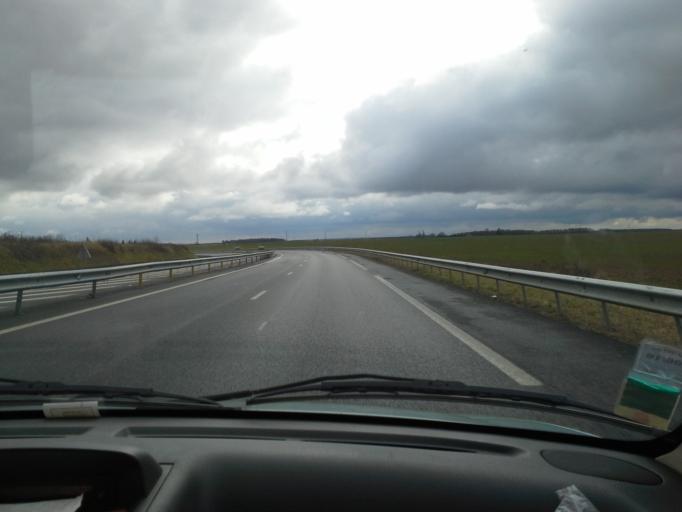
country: FR
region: Centre
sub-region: Departement du Loir-et-Cher
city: Saint-Sulpice-de-Pommeray
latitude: 47.6711
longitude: 1.2319
